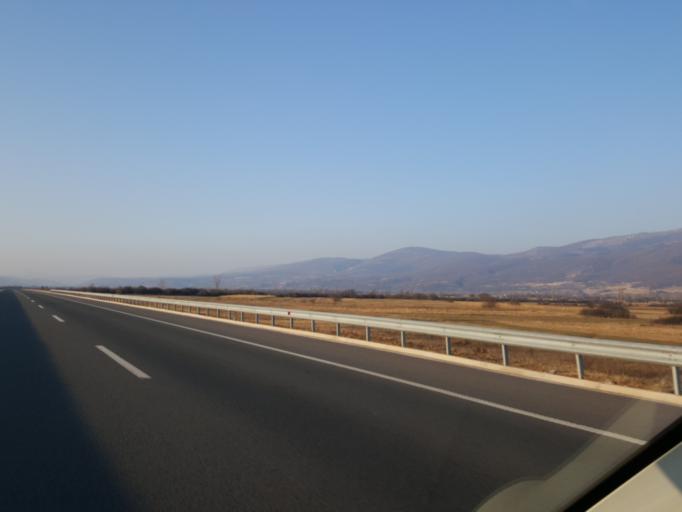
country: RS
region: Central Serbia
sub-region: Pirotski Okrug
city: Pirot
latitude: 43.0799
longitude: 22.6647
